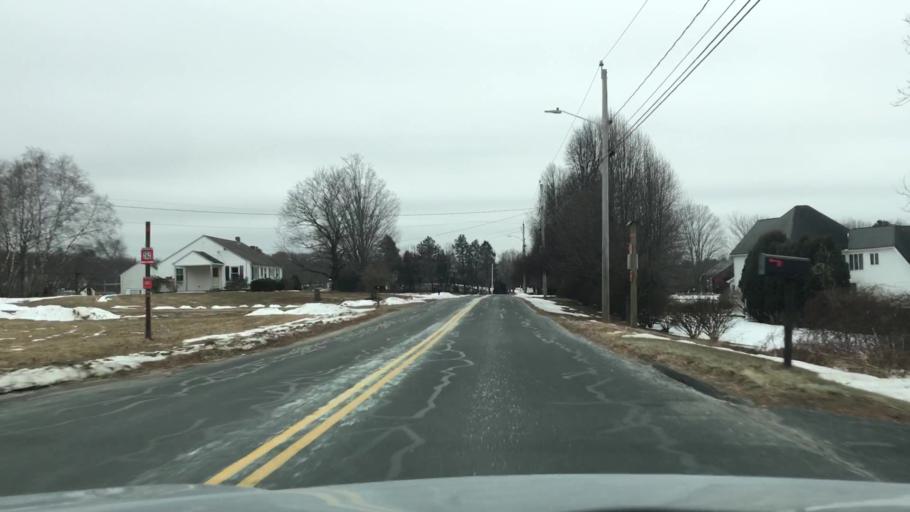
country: US
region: Massachusetts
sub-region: Hampden County
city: Westfield
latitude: 42.0857
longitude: -72.7158
